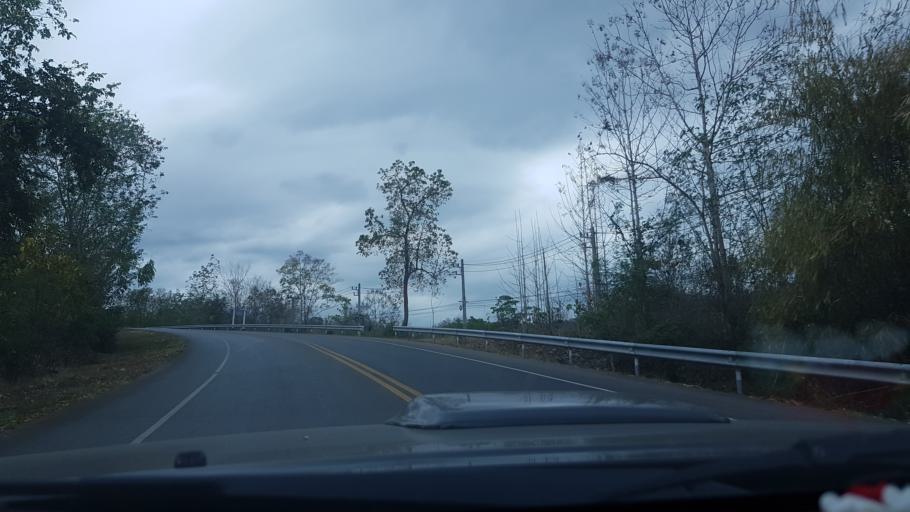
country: TH
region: Phetchabun
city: Phetchabun
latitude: 16.5327
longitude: 101.0974
